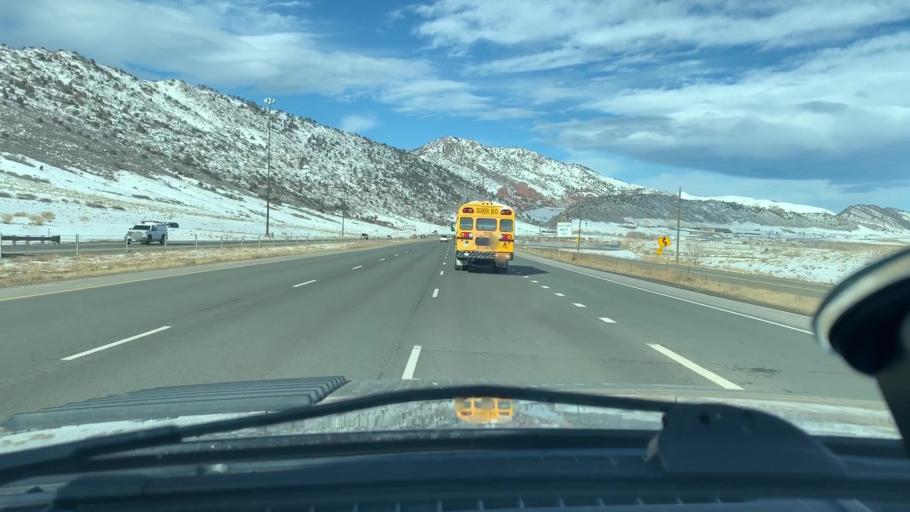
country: US
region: Colorado
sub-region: Jefferson County
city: Indian Hills
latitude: 39.6388
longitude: -105.1688
